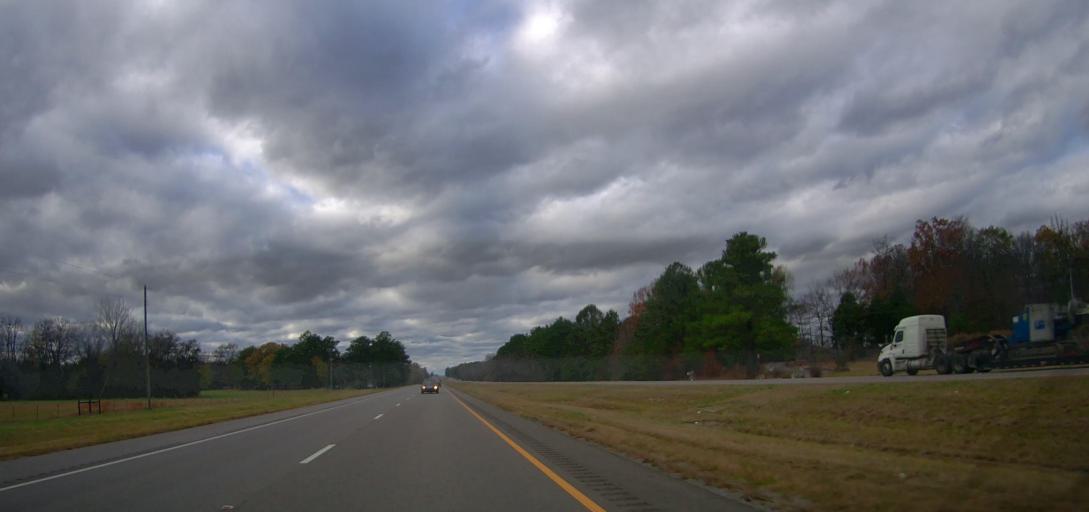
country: US
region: Alabama
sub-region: Morgan County
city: Danville
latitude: 34.3457
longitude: -87.0355
